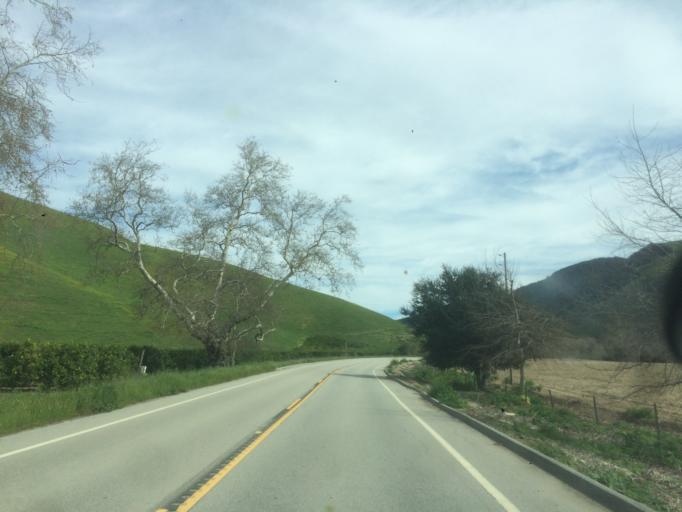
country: US
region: California
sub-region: San Luis Obispo County
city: Arroyo Grande
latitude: 35.1832
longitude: -120.5071
